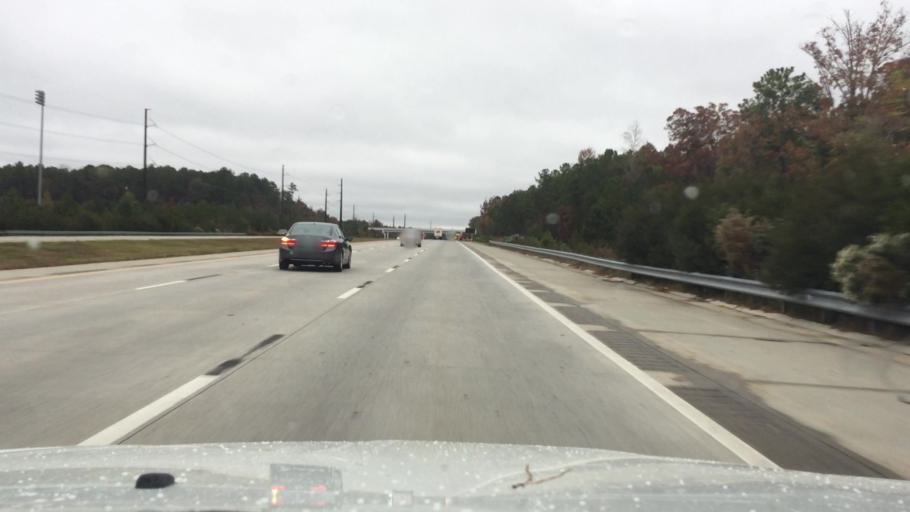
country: US
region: North Carolina
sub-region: Wake County
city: Green Level
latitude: 35.7966
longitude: -78.8895
